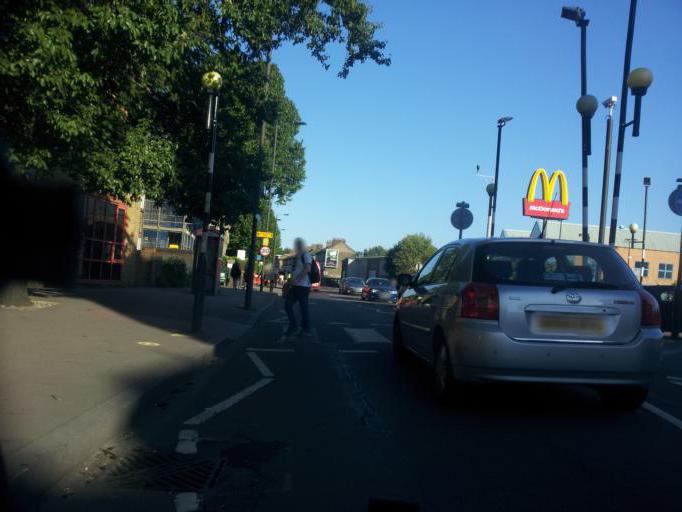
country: GB
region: England
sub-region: Greater London
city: Poplar
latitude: 51.4901
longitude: -0.0424
